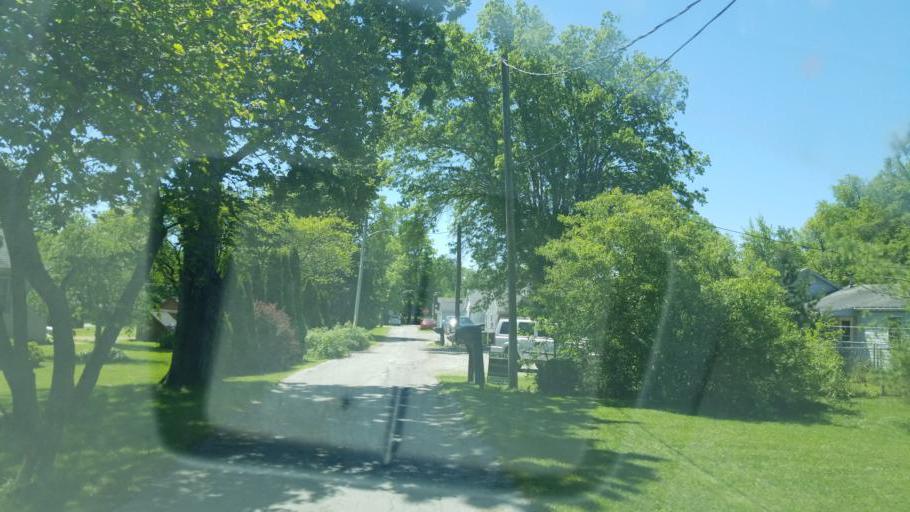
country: US
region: Ohio
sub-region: Shelby County
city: Fort Loramie
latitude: 40.3698
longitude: -84.3444
